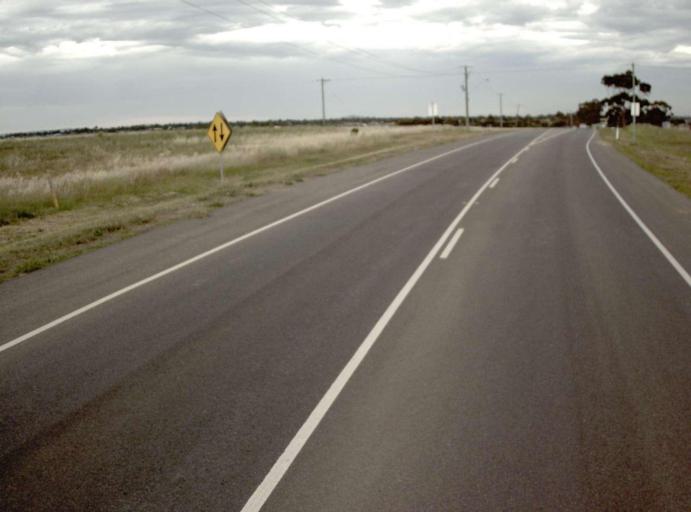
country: AU
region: Victoria
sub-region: Melton
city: Brookfield
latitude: -37.6864
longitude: 144.5290
